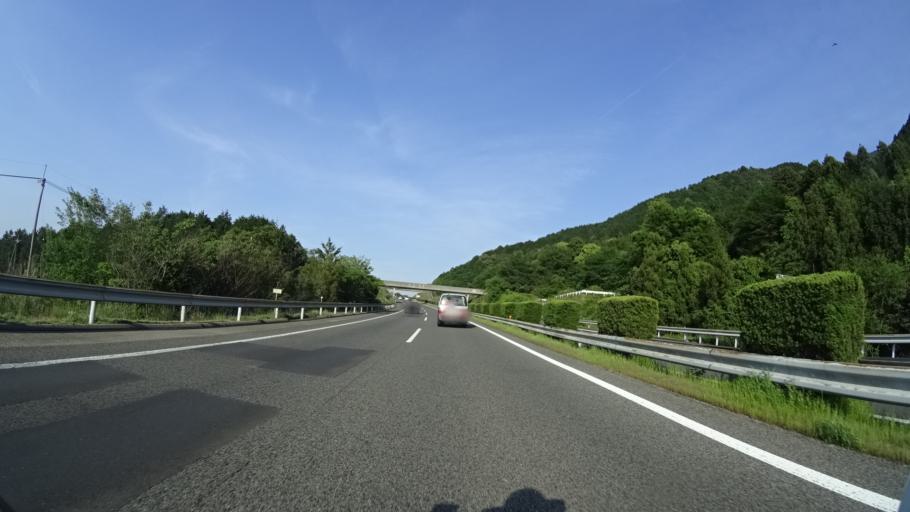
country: JP
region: Ehime
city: Niihama
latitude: 33.9507
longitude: 133.4351
